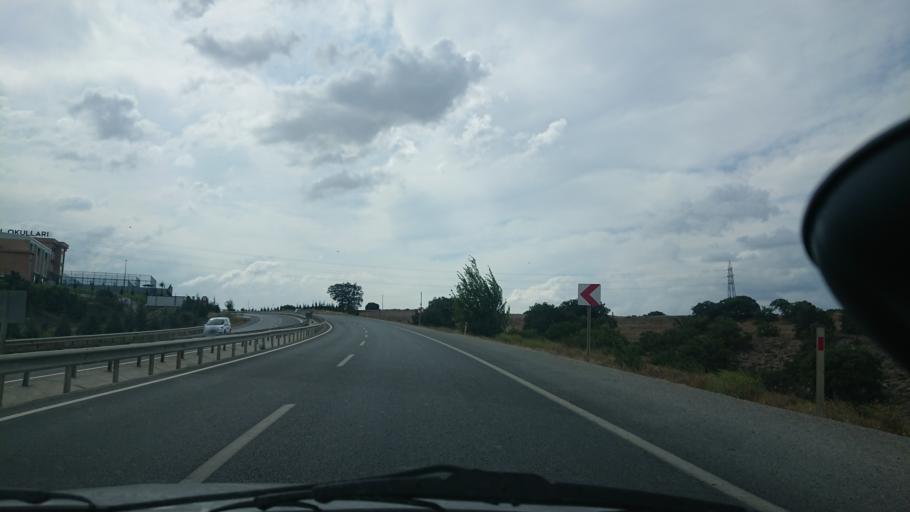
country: TR
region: Eskisehir
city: Eskisehir
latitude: 39.7424
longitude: 30.3974
